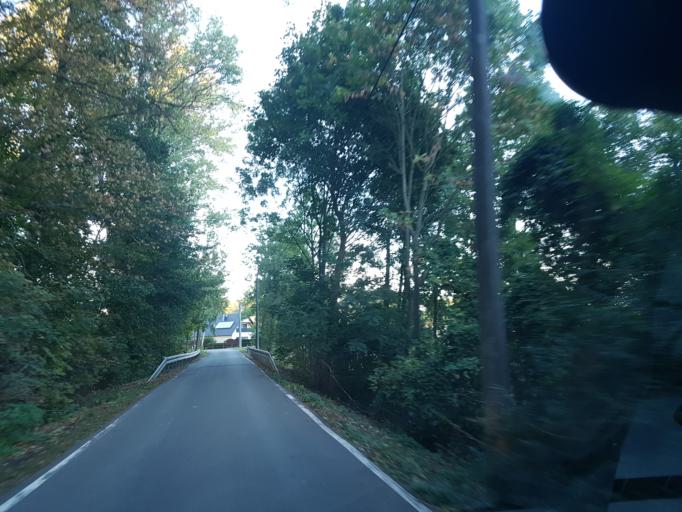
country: DE
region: Saxony
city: Naundorf
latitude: 51.2765
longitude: 13.1463
